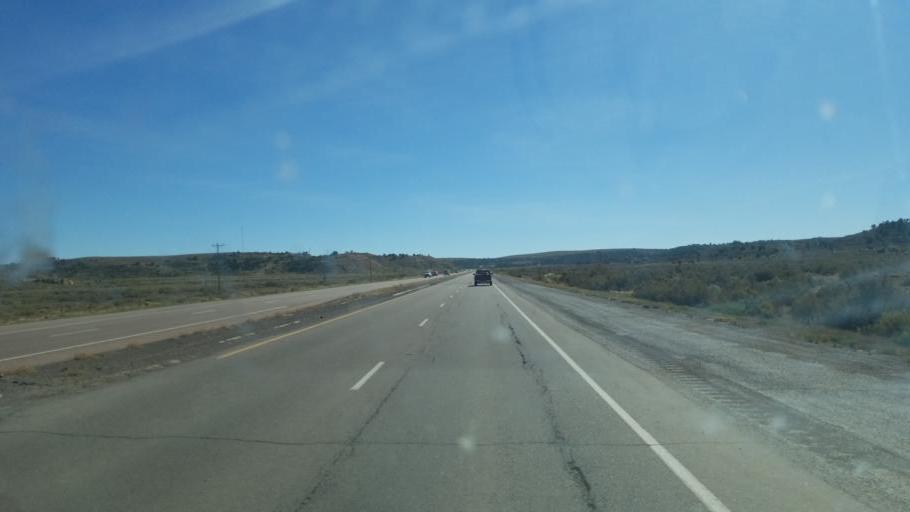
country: US
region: Arizona
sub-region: Apache County
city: Window Rock
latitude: 35.6462
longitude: -109.0301
